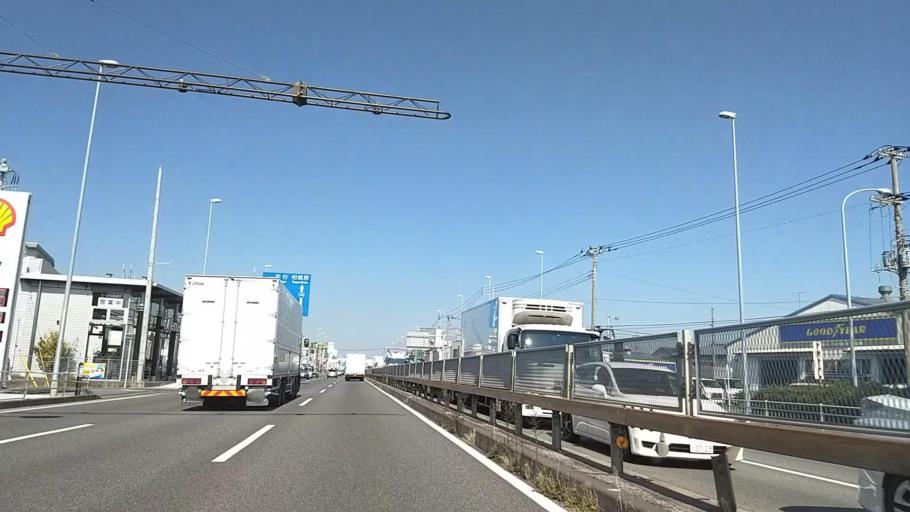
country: JP
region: Kanagawa
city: Atsugi
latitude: 35.4548
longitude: 139.3590
